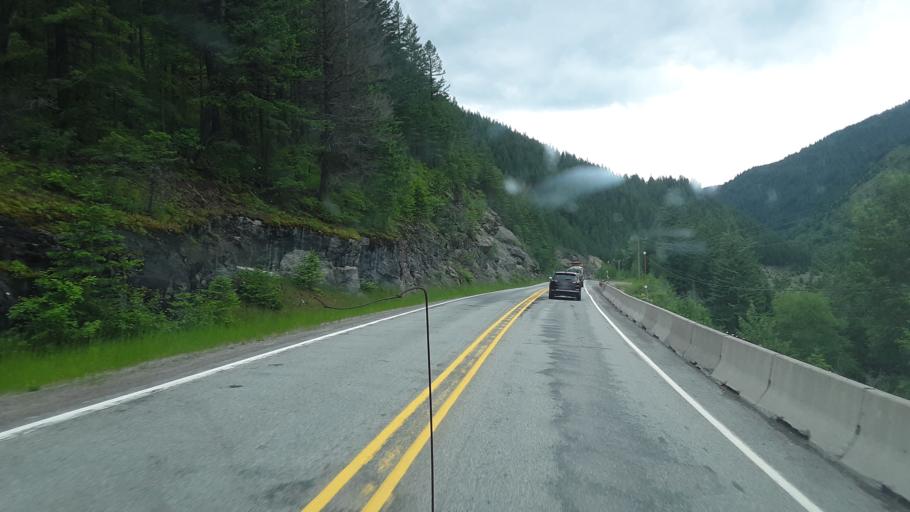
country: US
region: Montana
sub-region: Flathead County
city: Columbia Falls
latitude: 48.4925
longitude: -113.9101
